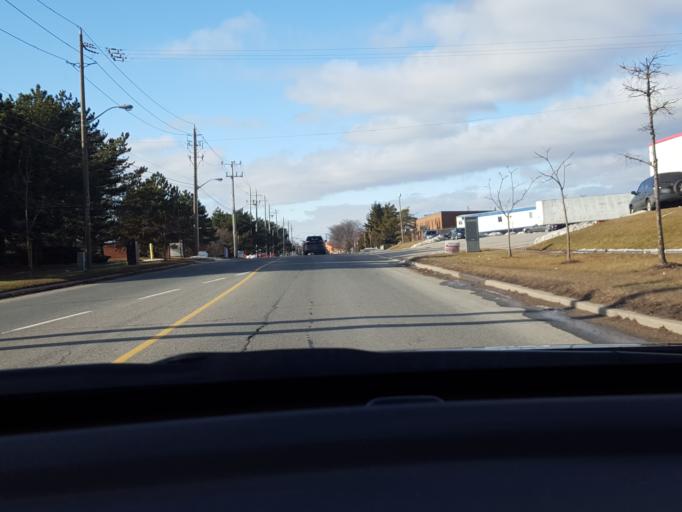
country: CA
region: Ontario
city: Concord
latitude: 43.7627
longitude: -79.5565
